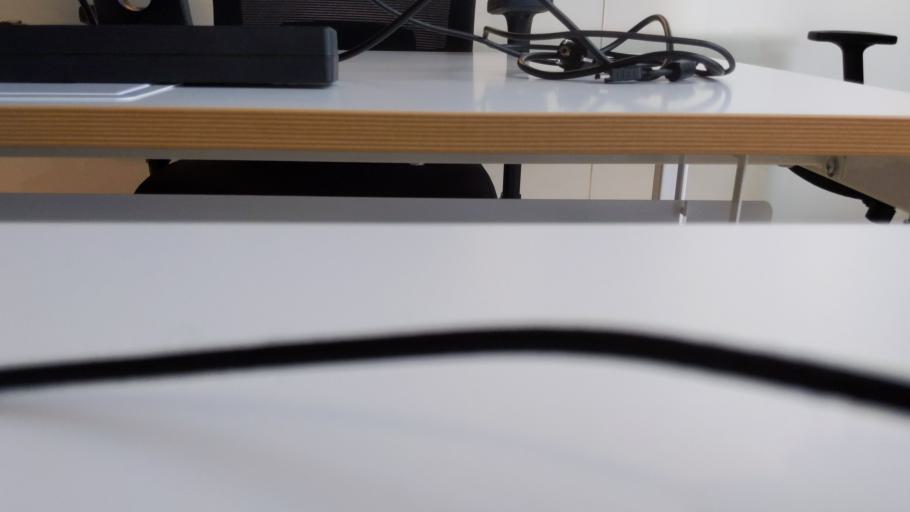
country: RU
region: Moskovskaya
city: Shevlyakovo
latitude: 56.3877
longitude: 36.8615
